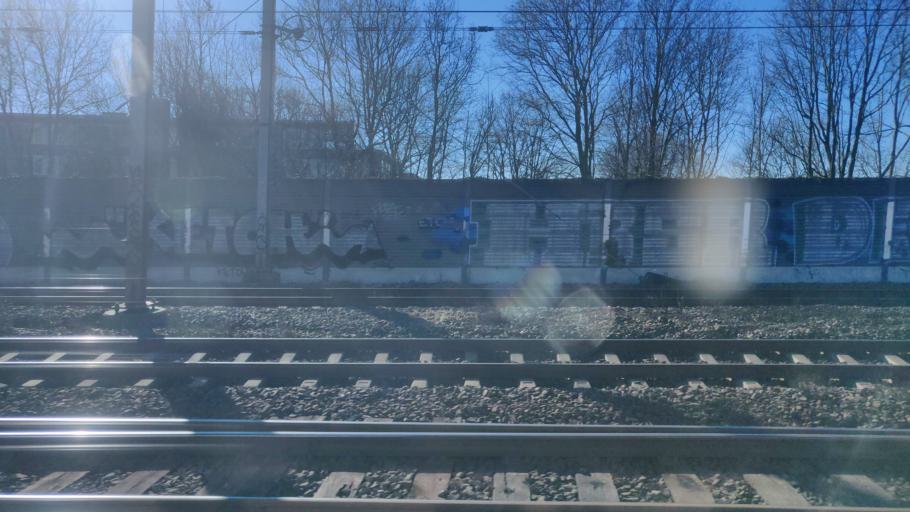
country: NL
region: North Holland
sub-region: Gemeente Weesp
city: Weesp
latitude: 52.3161
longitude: 5.0368
